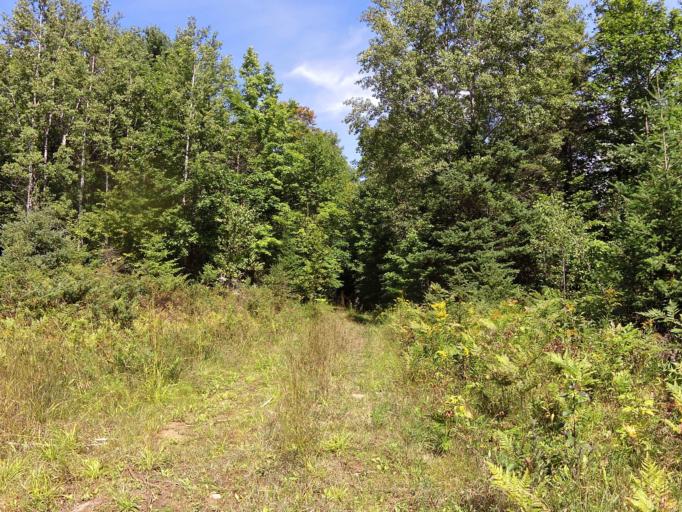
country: CA
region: Ontario
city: Renfrew
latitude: 45.0270
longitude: -76.7036
